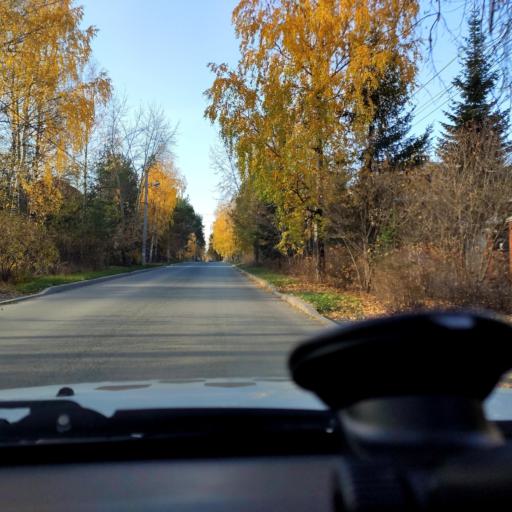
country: RU
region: Perm
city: Perm
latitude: 58.0535
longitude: 56.2952
